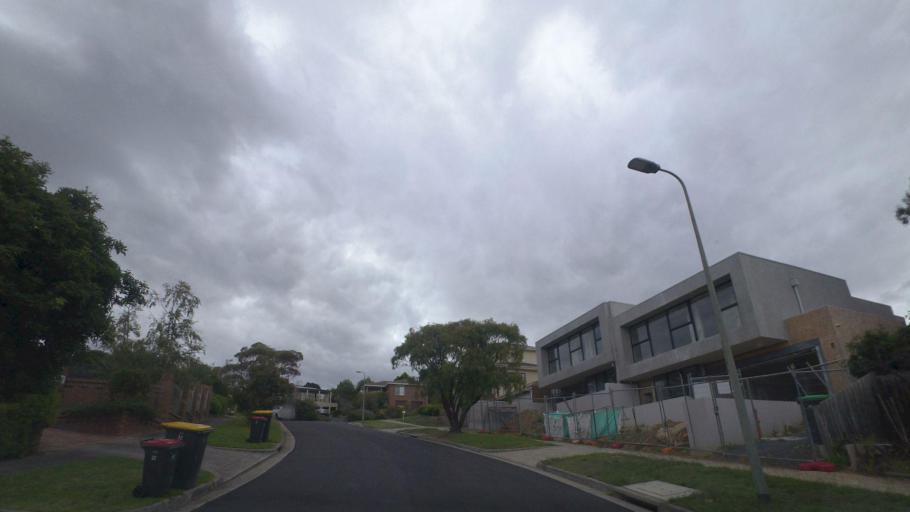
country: AU
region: Victoria
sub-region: Nillumbik
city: Eltham
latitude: -37.7537
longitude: 145.1592
